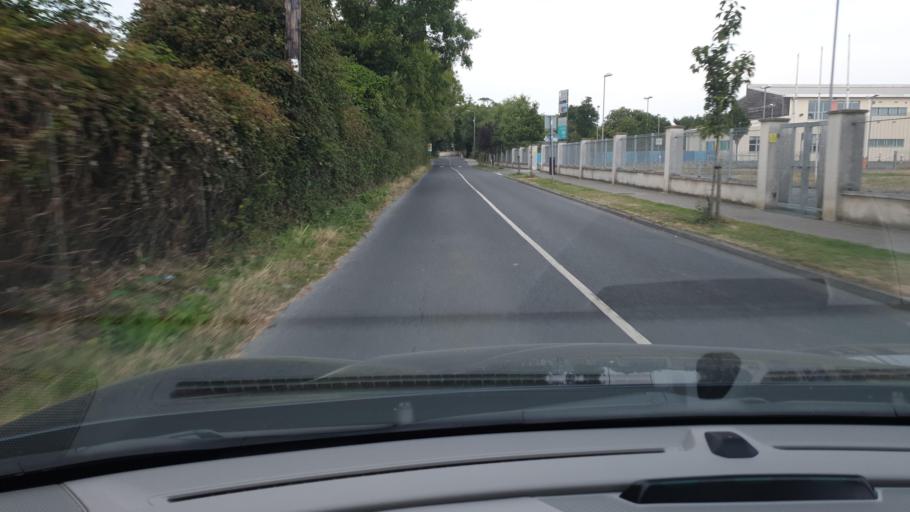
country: IE
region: Leinster
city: Donabate
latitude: 53.4911
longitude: -6.1468
